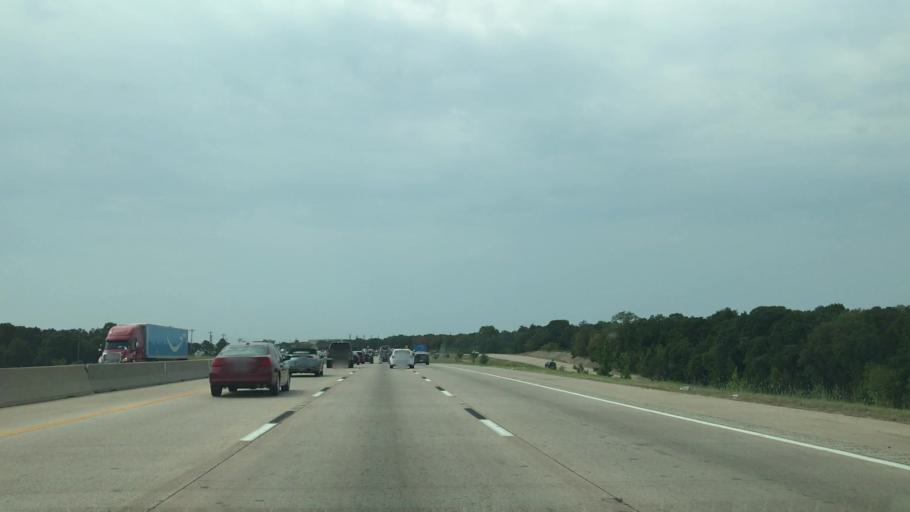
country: US
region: Texas
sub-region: Tarrant County
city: Southlake
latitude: 32.9696
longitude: -97.1585
